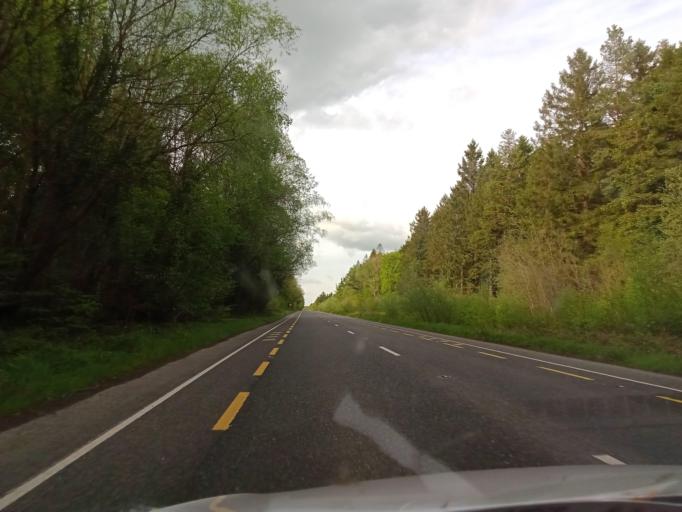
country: IE
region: Leinster
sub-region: Laois
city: Abbeyleix
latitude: 52.8938
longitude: -7.3619
